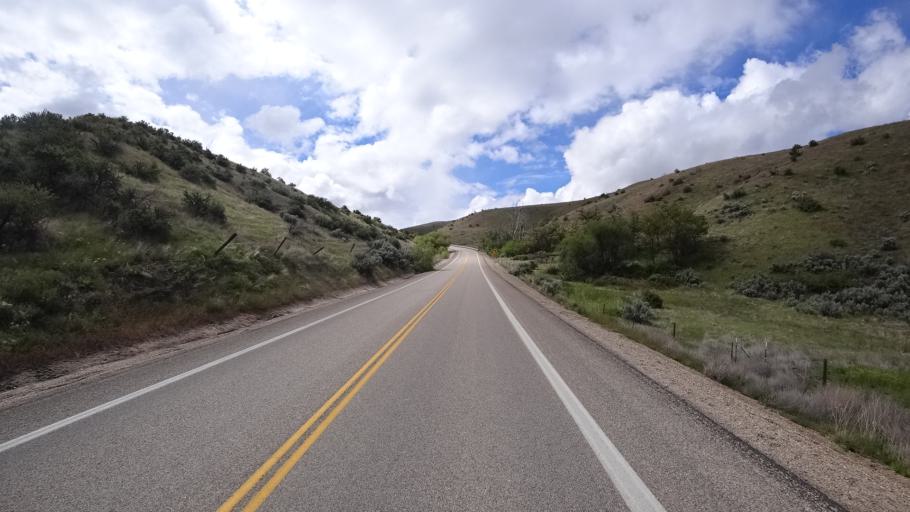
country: US
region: Idaho
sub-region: Ada County
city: Garden City
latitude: 43.6988
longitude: -116.2288
